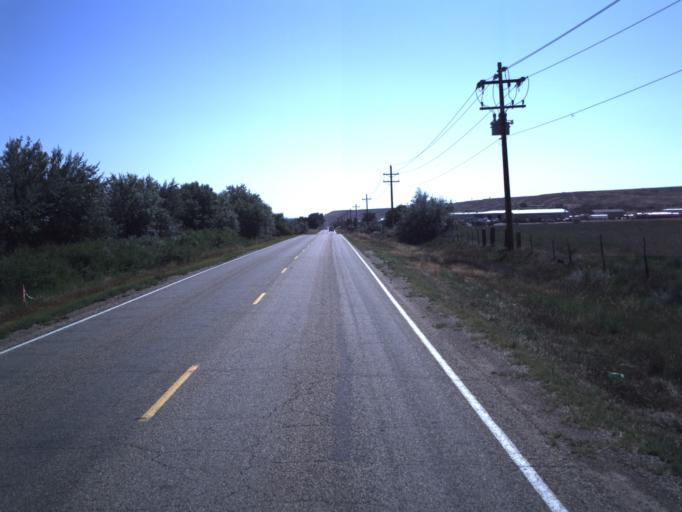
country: US
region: Utah
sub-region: Duchesne County
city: Roosevelt
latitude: 40.2585
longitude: -110.0834
